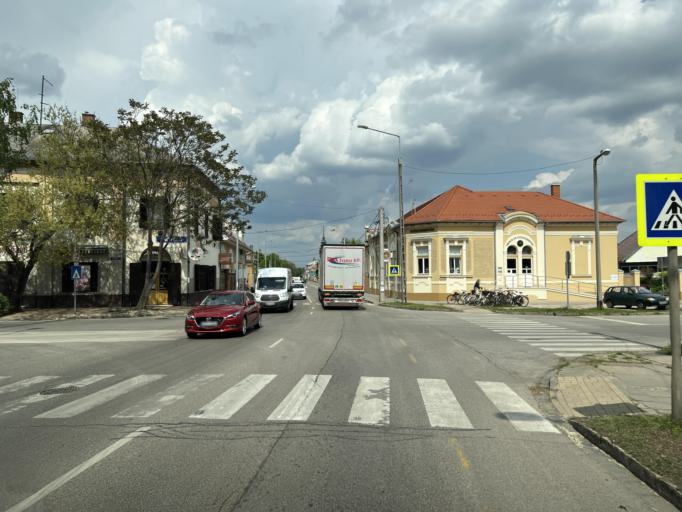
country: HU
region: Pest
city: Nagykoros
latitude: 47.0287
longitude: 19.7810
